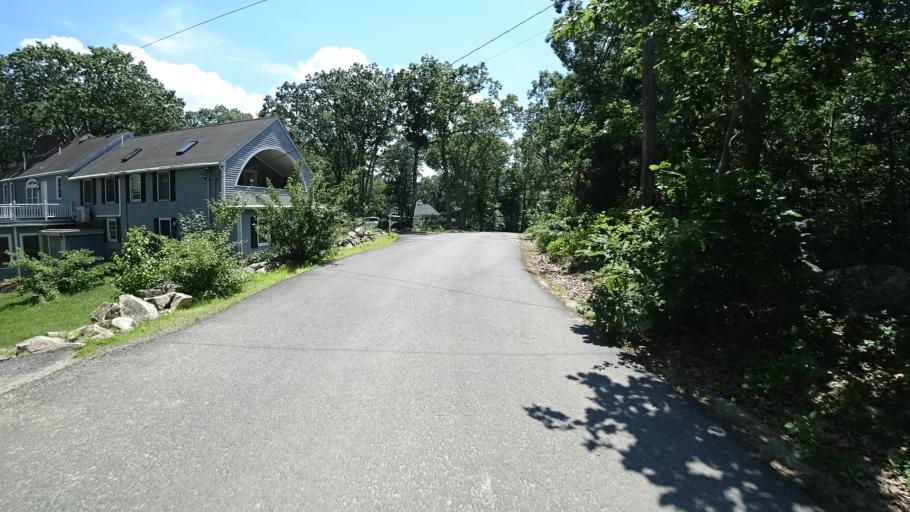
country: US
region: Massachusetts
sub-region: Norfolk County
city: Needham
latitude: 42.2560
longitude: -71.2150
